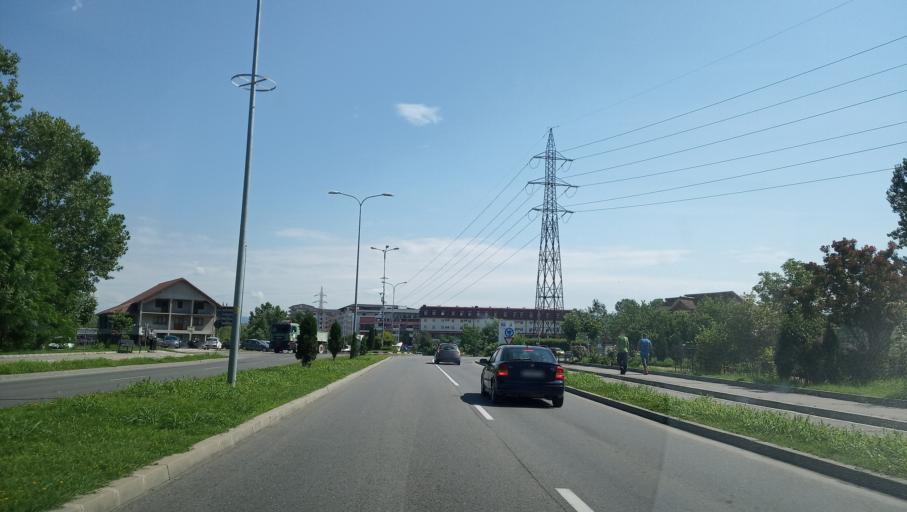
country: RO
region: Valcea
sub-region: Municipiul Ramnicu Valcea
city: Ramnicu Valcea
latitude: 45.0799
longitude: 24.3649
